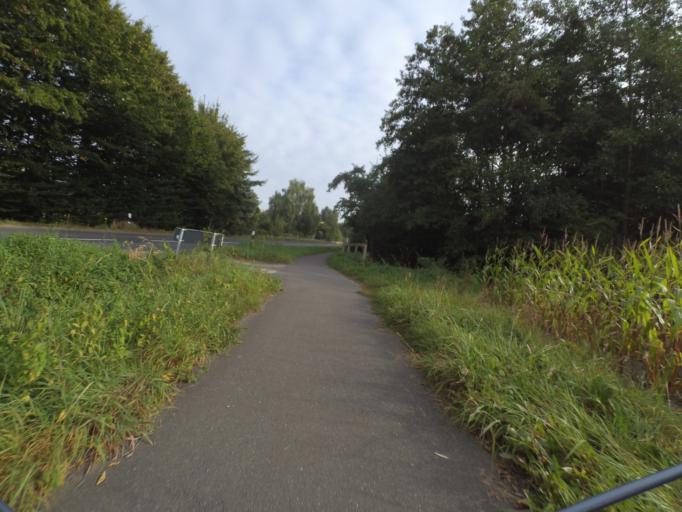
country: DE
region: Lower Saxony
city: Bad Bentheim
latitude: 52.3077
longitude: 7.0990
